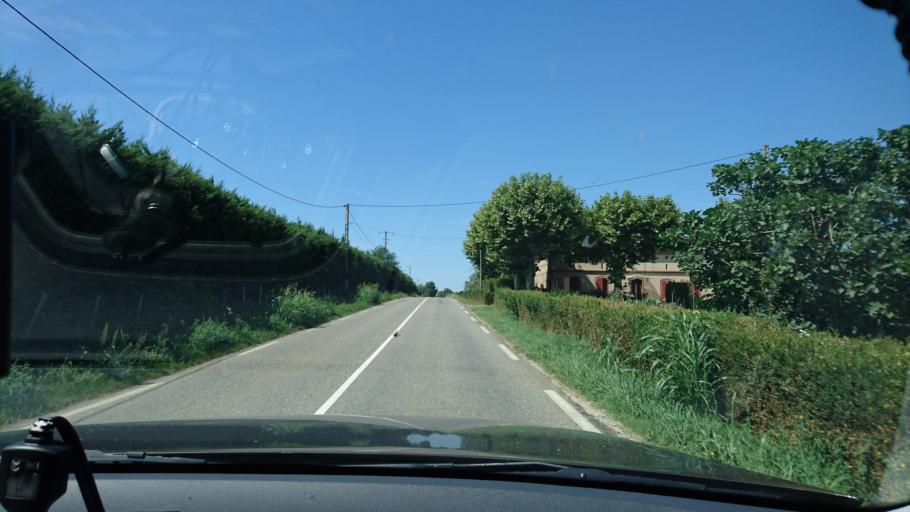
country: FR
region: Midi-Pyrenees
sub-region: Departement de l'Ariege
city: Lezat-sur-Leze
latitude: 43.2574
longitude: 1.3591
